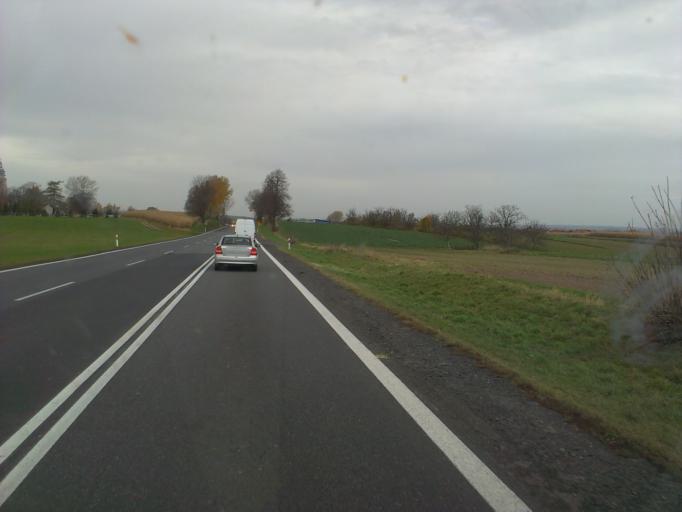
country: PL
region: Subcarpathian Voivodeship
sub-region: Powiat lancucki
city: Kosina
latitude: 50.0711
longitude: 22.3398
